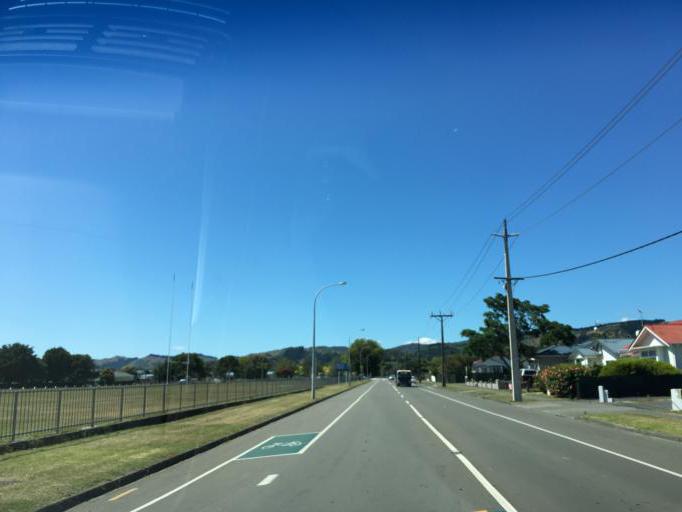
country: NZ
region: Gisborne
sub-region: Gisborne District
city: Gisborne
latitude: -38.6586
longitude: 178.0087
